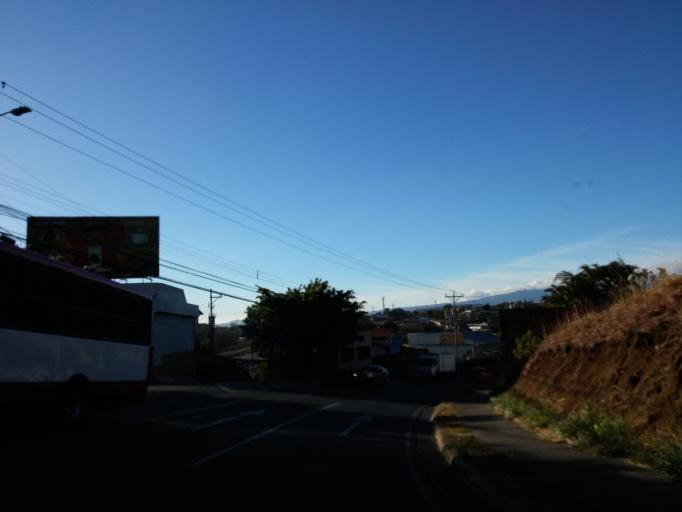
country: CR
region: Alajuela
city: Alajuela
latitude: 10.0016
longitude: -84.2008
